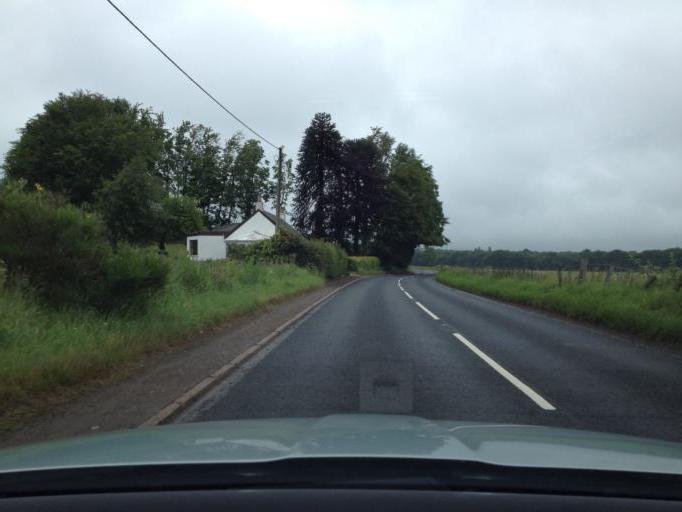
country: GB
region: Scotland
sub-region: Angus
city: Brechin
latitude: 56.8190
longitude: -2.6590
